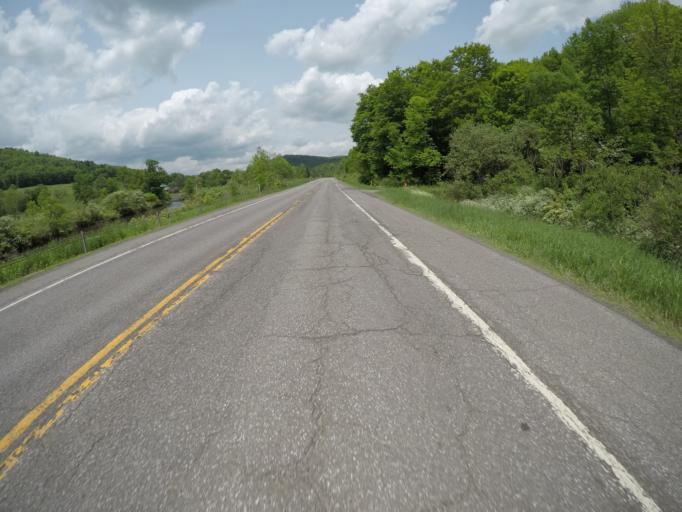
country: US
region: New York
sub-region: Delaware County
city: Stamford
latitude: 42.2199
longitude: -74.5923
